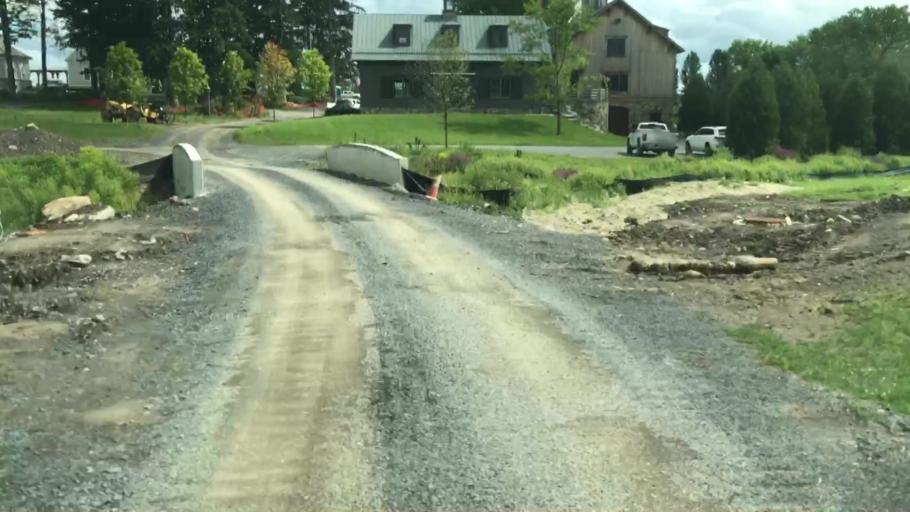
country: US
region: New York
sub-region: Onondaga County
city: Skaneateles
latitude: 42.9333
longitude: -76.4310
